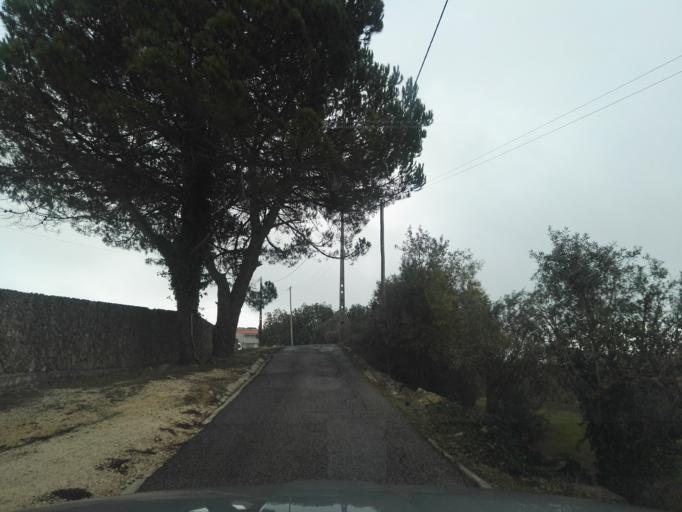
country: PT
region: Lisbon
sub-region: Vila Franca de Xira
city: Sao Joao dos Montes
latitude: 38.9663
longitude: -9.0215
